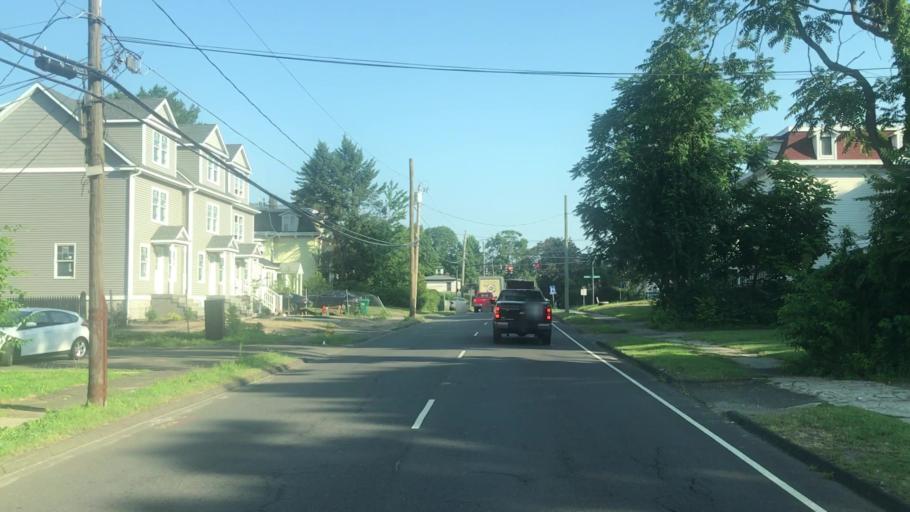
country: US
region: Connecticut
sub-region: Fairfield County
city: Danbury
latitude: 41.3990
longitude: -73.4520
